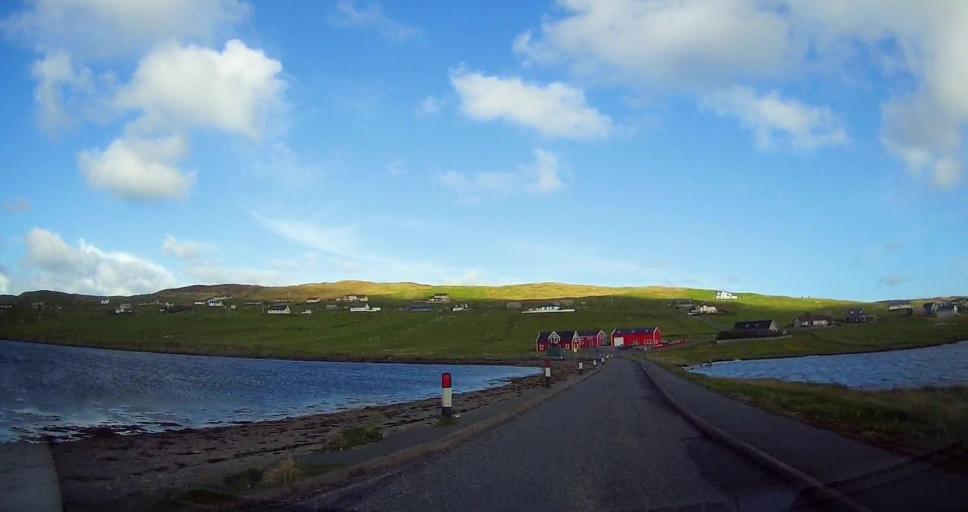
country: GB
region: Scotland
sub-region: Shetland Islands
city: Shetland
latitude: 60.3699
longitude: -1.1325
